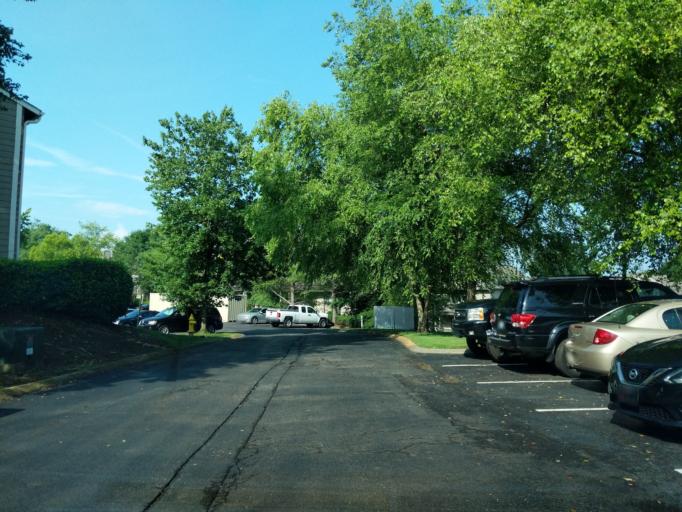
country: US
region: Tennessee
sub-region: Sumner County
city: Hendersonville
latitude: 36.3112
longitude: -86.6526
